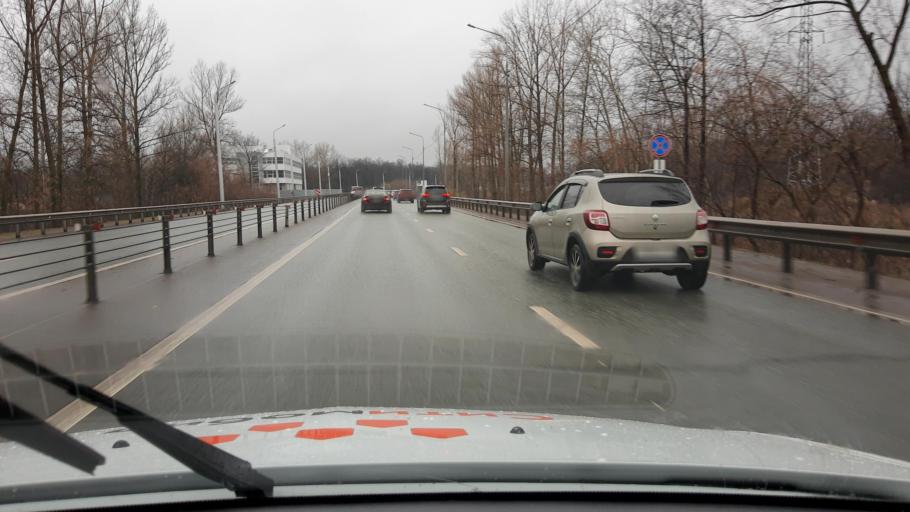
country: RU
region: Bashkortostan
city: Ufa
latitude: 54.6992
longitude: 55.8973
